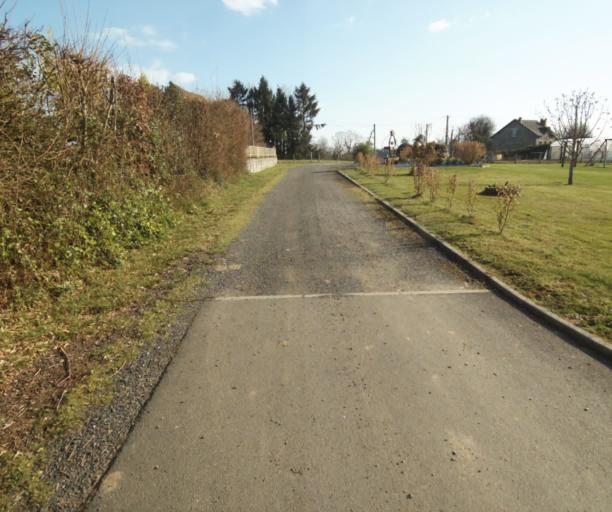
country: FR
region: Limousin
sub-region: Departement de la Correze
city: Saint-Mexant
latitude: 45.3396
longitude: 1.5950
